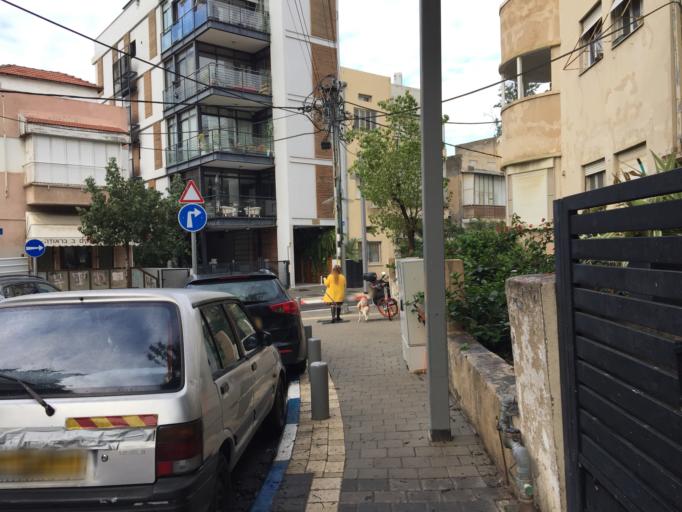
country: IL
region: Tel Aviv
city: Tel Aviv
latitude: 32.0665
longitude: 34.7729
